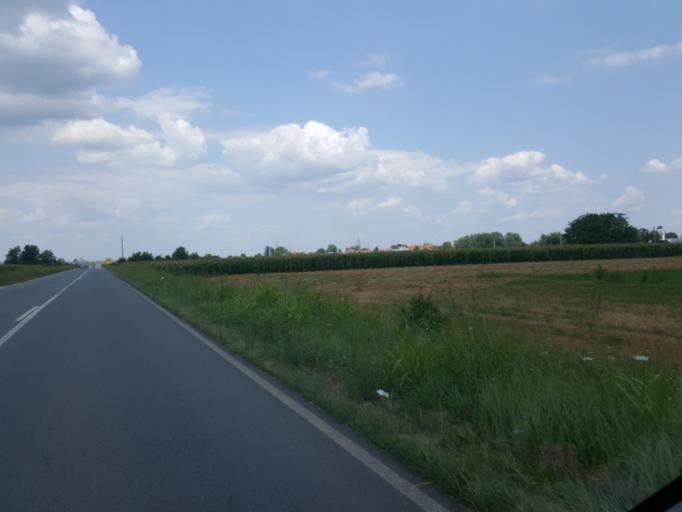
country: RS
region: Autonomna Pokrajina Vojvodina
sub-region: Sremski Okrug
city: Pecinci
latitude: 44.9109
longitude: 19.9566
